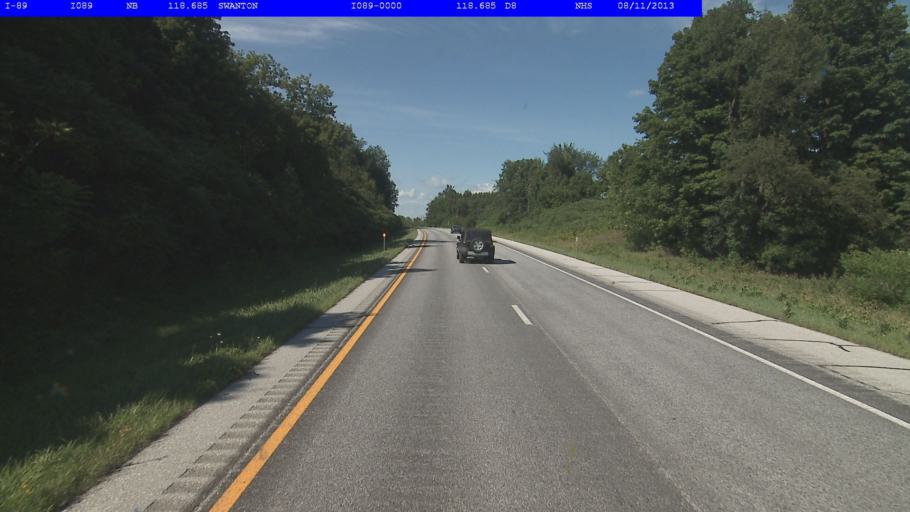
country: US
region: Vermont
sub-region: Franklin County
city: Saint Albans
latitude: 44.8581
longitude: -73.0805
